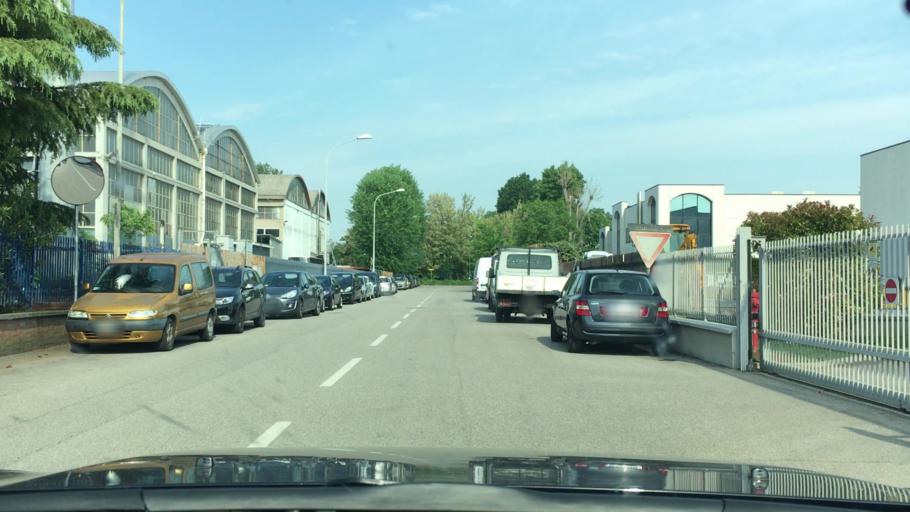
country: IT
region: Emilia-Romagna
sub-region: Provincia di Bologna
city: Quarto Inferiore
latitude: 44.5516
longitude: 11.3928
